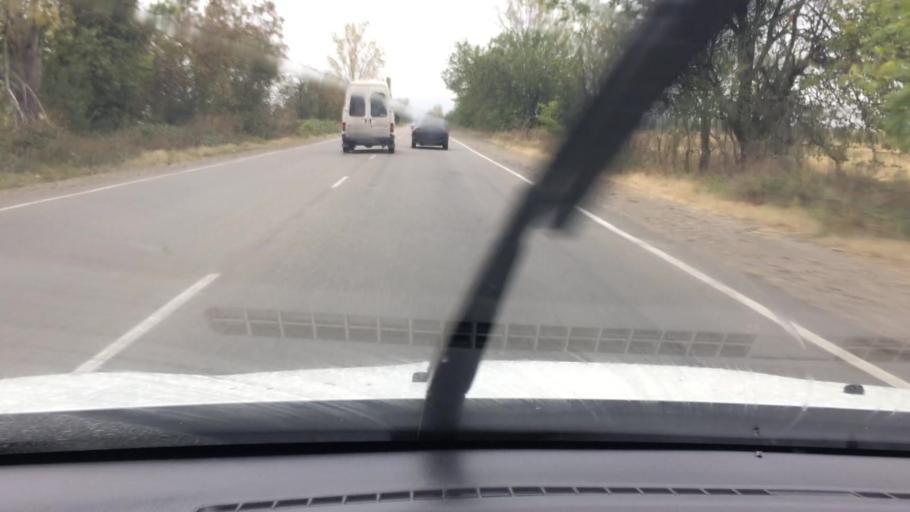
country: GE
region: Kvemo Kartli
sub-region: Marneuli
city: Marneuli
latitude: 41.5533
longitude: 44.7763
